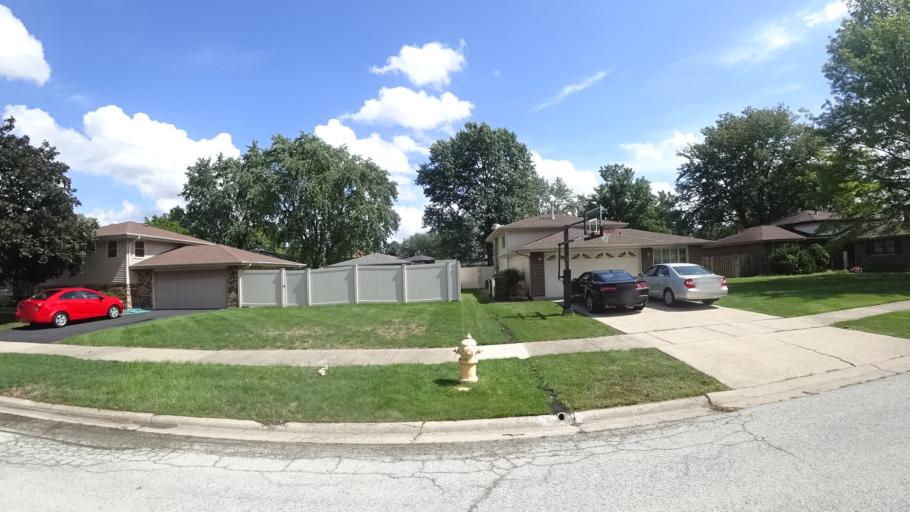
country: US
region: Illinois
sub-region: Cook County
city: Tinley Park
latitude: 41.5638
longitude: -87.7779
